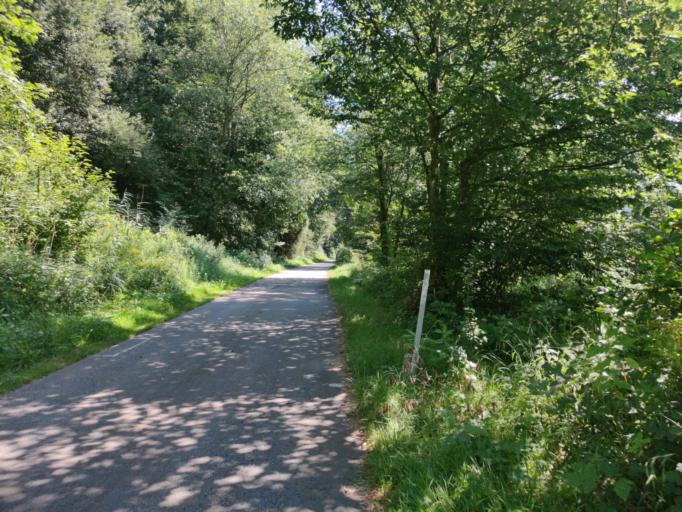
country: AT
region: Upper Austria
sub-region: Politischer Bezirk Rohrbach
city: Pfarrkirchen im Muehlkreis
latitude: 48.4412
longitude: 13.8403
